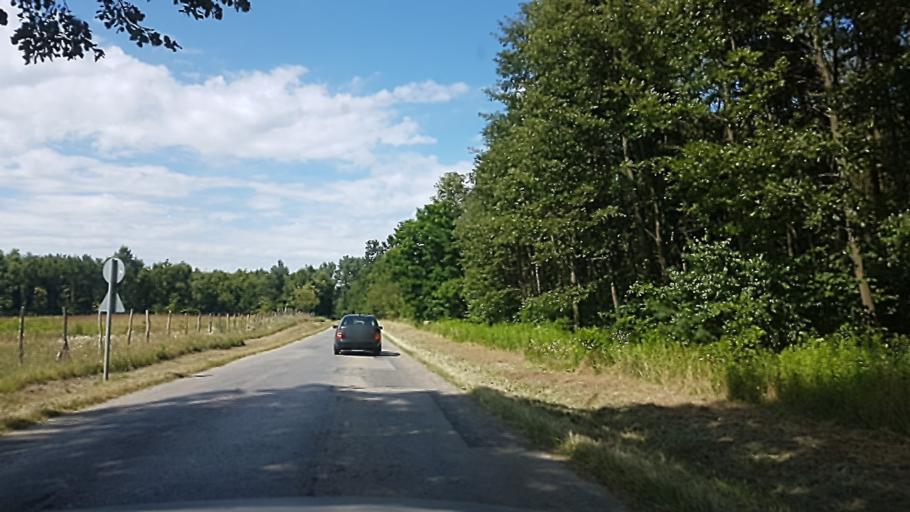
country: HU
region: Somogy
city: Barcs
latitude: 45.9626
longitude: 17.5890
